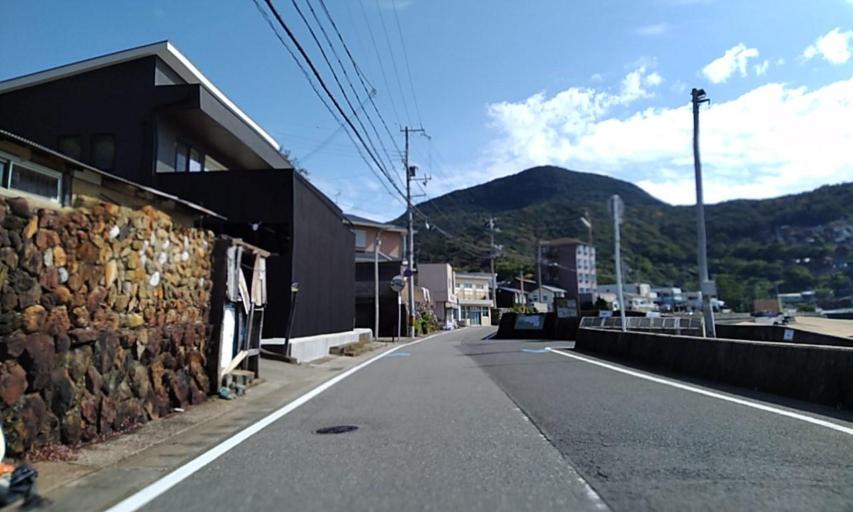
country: JP
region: Wakayama
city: Gobo
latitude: 33.9698
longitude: 135.0852
